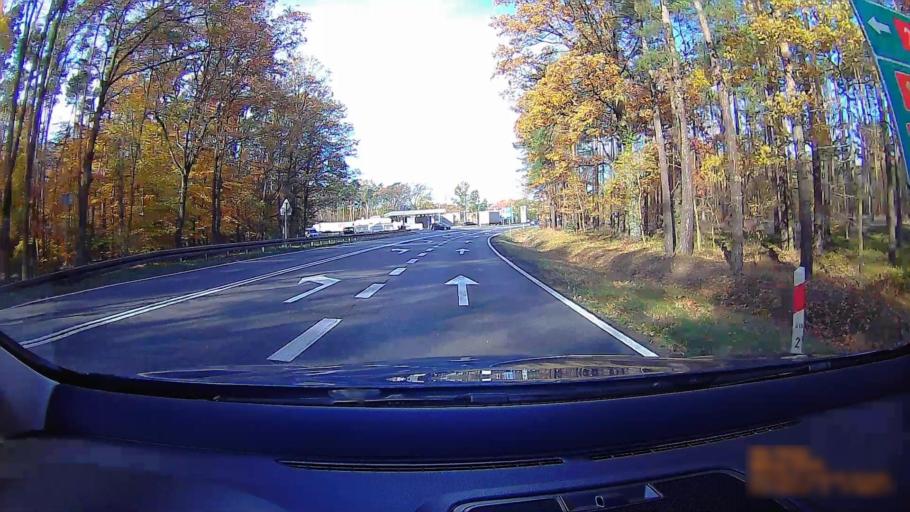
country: PL
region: Greater Poland Voivodeship
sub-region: Powiat ostrowski
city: Przygodzice
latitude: 51.5087
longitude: 17.8466
